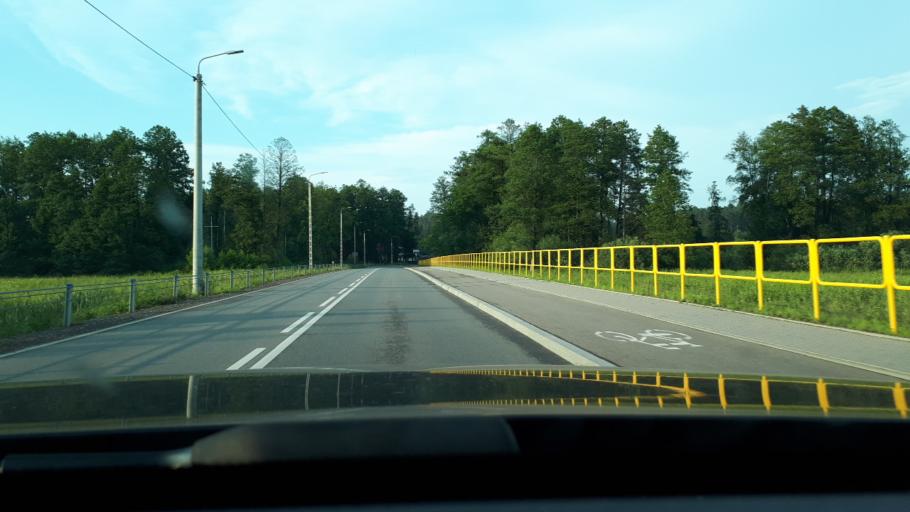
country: PL
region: Podlasie
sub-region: Powiat bialostocki
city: Suprasl
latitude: 53.2165
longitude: 23.3399
